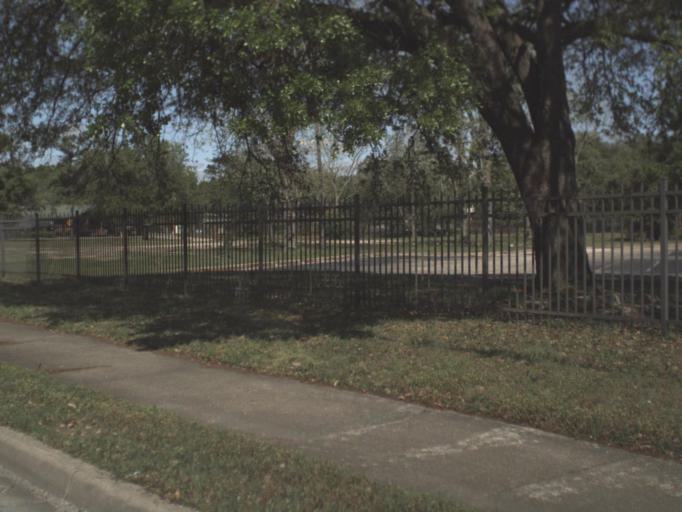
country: US
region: Florida
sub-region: Escambia County
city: Ferry Pass
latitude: 30.5164
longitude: -87.2159
